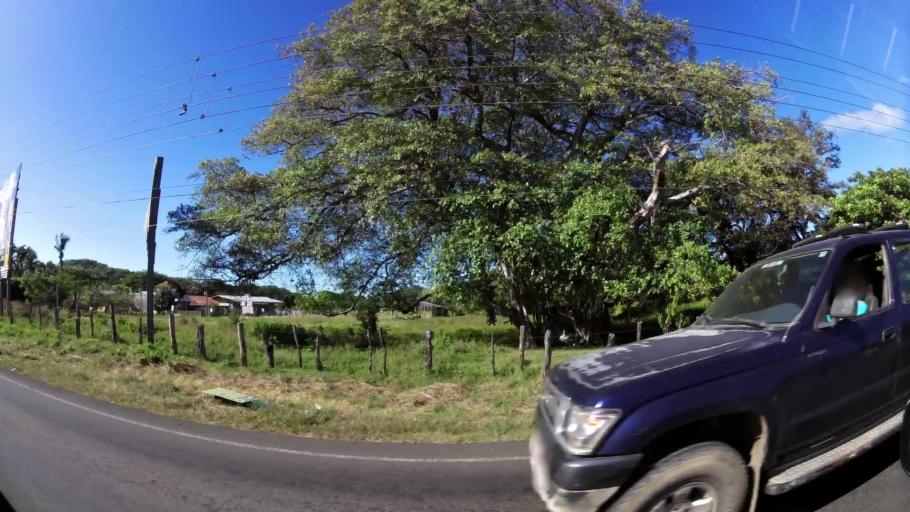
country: CR
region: Guanacaste
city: Belen
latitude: 10.3705
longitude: -85.7812
